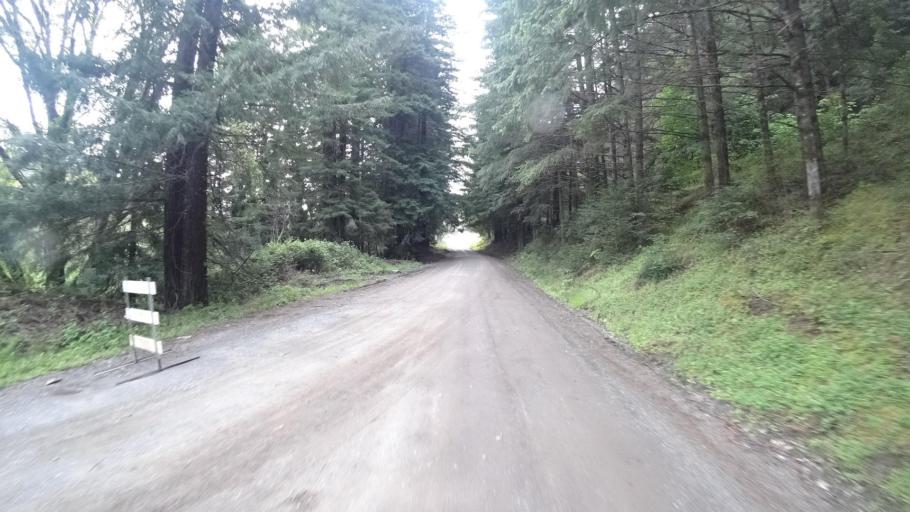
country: US
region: California
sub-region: Humboldt County
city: Redway
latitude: 40.3255
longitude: -123.8389
